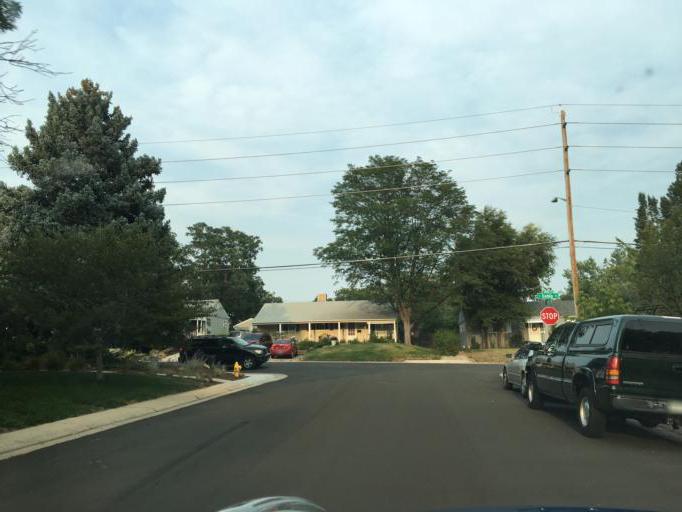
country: US
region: Colorado
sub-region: Arapahoe County
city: Glendale
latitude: 39.6835
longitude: -104.9322
